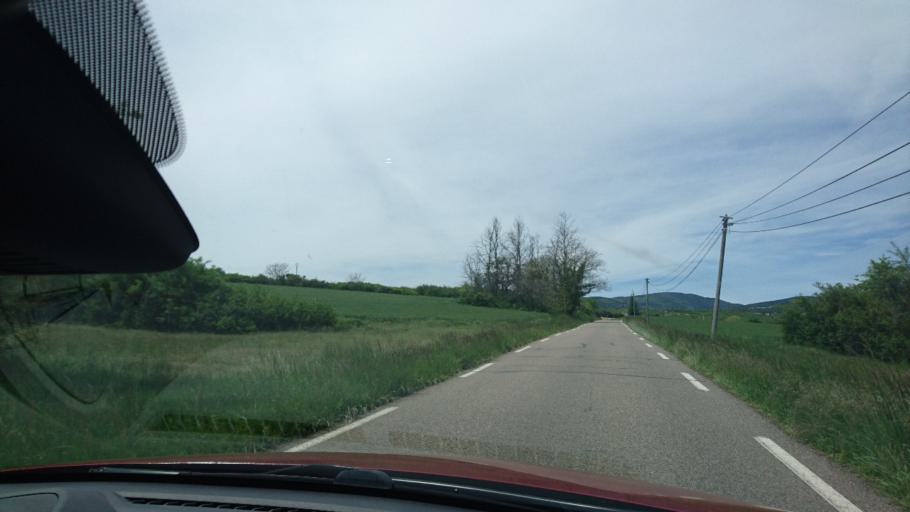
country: FR
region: Provence-Alpes-Cote d'Azur
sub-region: Departement du Vaucluse
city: Sault
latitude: 44.0976
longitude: 5.4051
